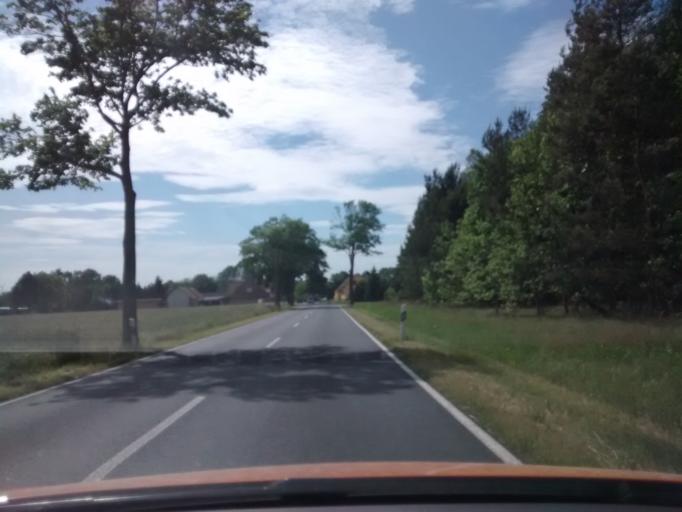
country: DE
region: Brandenburg
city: Juterbog
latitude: 51.9858
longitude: 13.1806
